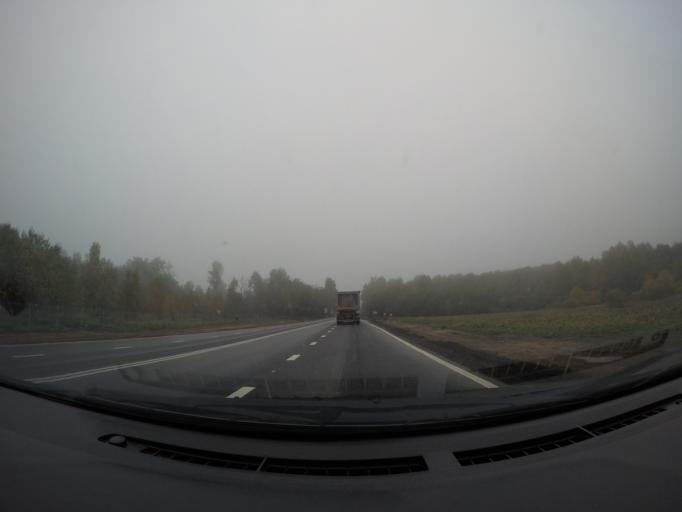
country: RU
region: Moskovskaya
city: Rumyantsevo
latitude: 55.8635
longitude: 36.5335
